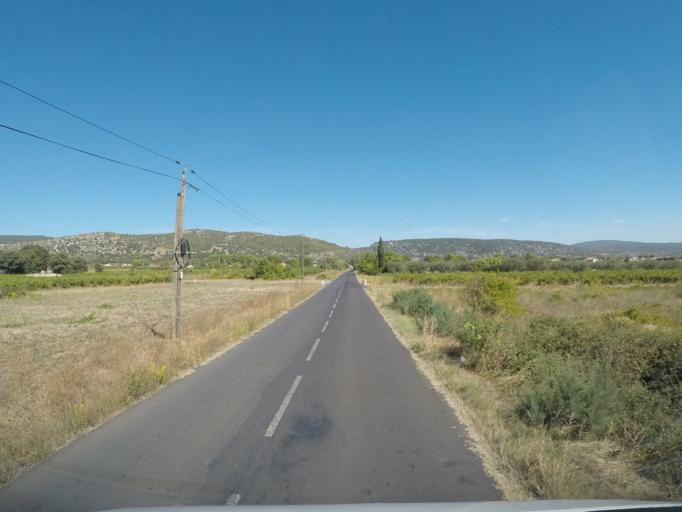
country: FR
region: Languedoc-Roussillon
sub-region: Departement de l'Herault
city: Saint-Jean-de-Fos
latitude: 43.6923
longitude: 3.5453
